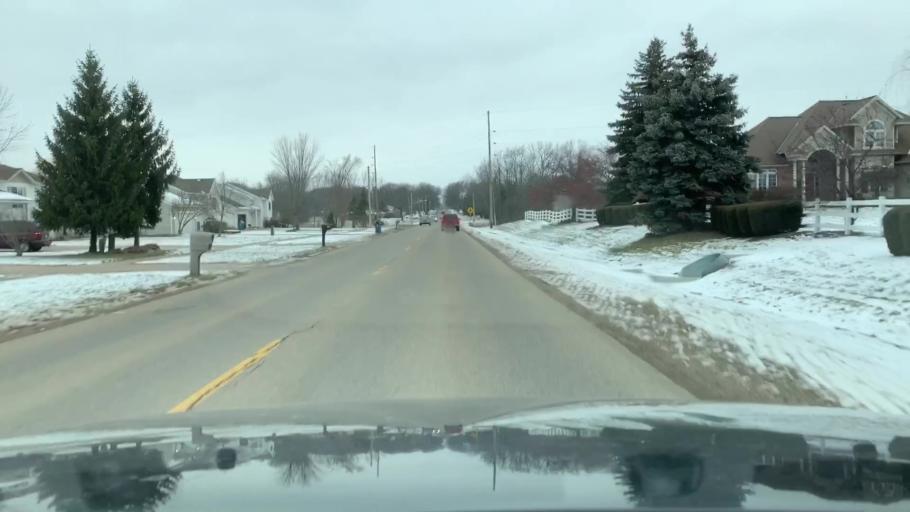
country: US
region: Michigan
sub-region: Ottawa County
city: Zeeland
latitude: 42.7962
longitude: -86.0382
